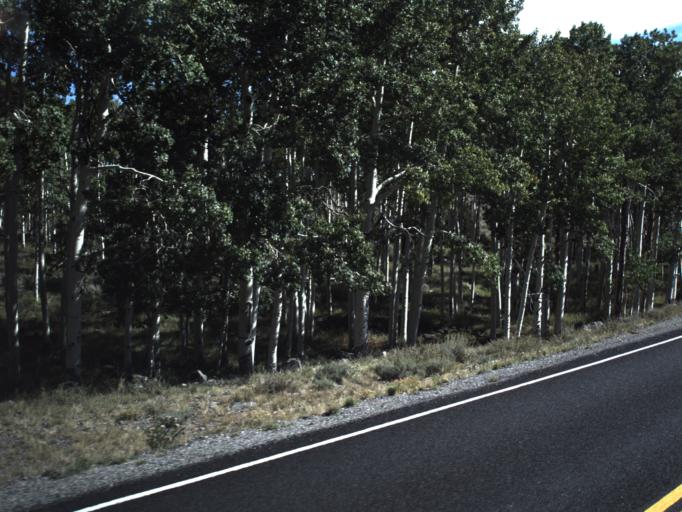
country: US
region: Utah
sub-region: Wayne County
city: Loa
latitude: 38.5157
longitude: -111.7615
